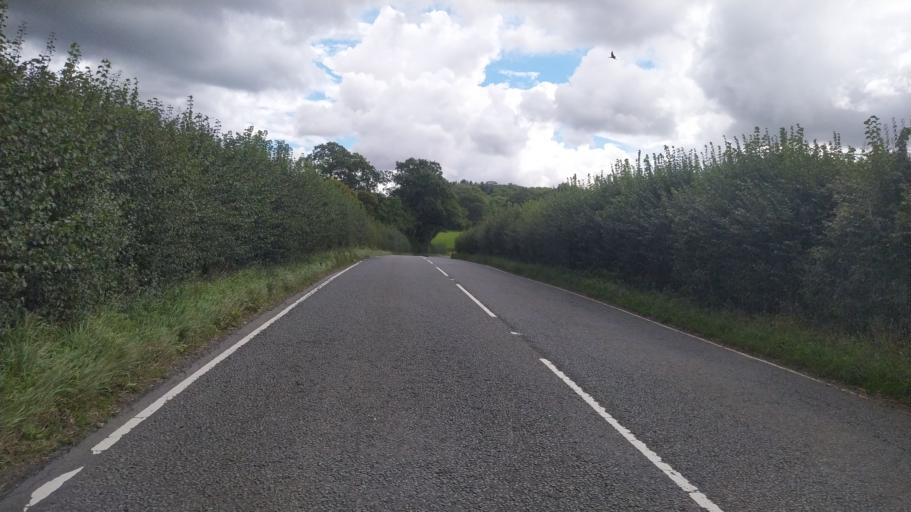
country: GB
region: England
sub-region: Dorset
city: Sturminster Newton
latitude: 50.9201
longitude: -2.2990
